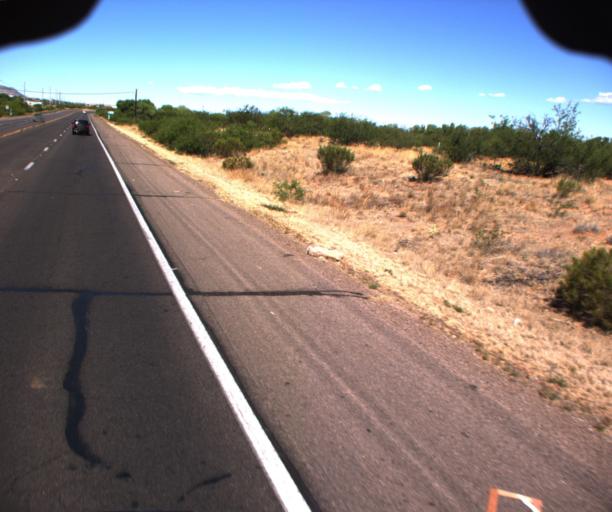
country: US
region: Arizona
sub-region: Cochise County
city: Sierra Vista
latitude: 31.5695
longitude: -110.2995
